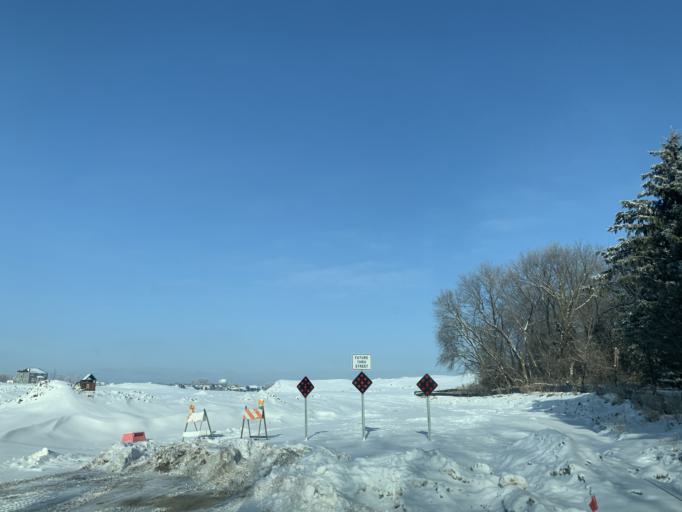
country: US
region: Minnesota
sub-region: Dakota County
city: Lakeville
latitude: 44.6597
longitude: -93.2274
